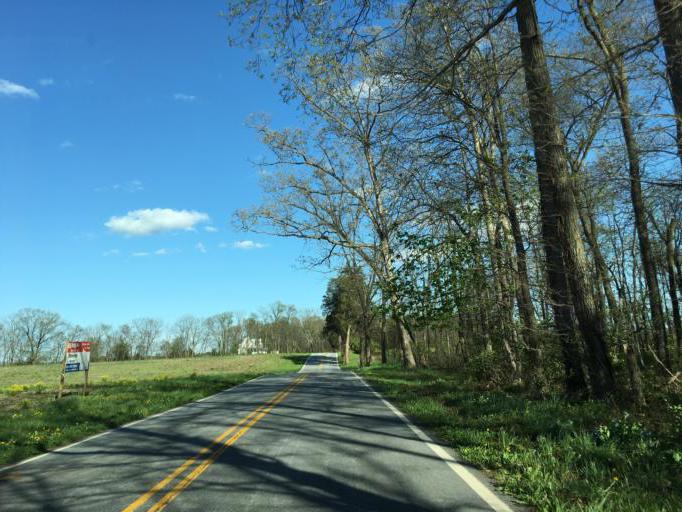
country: US
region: Maryland
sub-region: Frederick County
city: Emmitsburg
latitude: 39.6384
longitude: -77.2912
